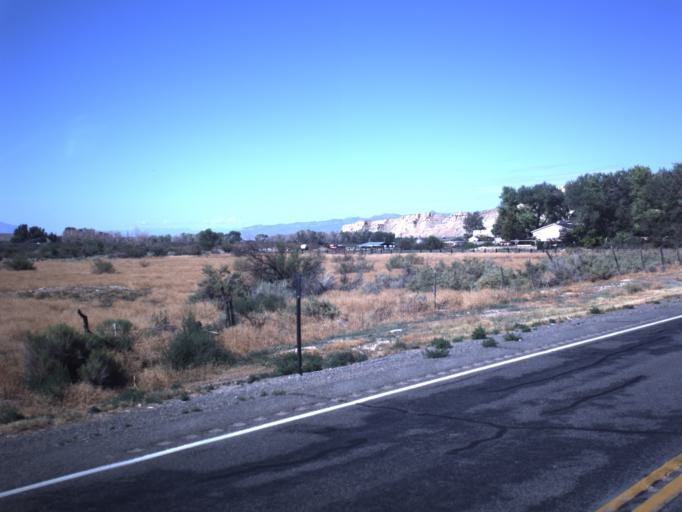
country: US
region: Utah
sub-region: Sanpete County
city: Gunnison
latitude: 39.1590
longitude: -111.7550
